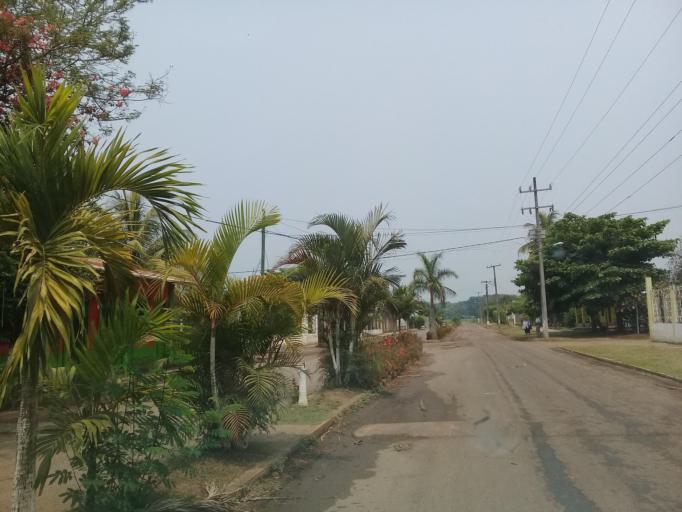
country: MX
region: Veracruz
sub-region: Tezonapa
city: Laguna Chica (Pueblo Nuevo)
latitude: 18.5176
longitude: -96.7217
